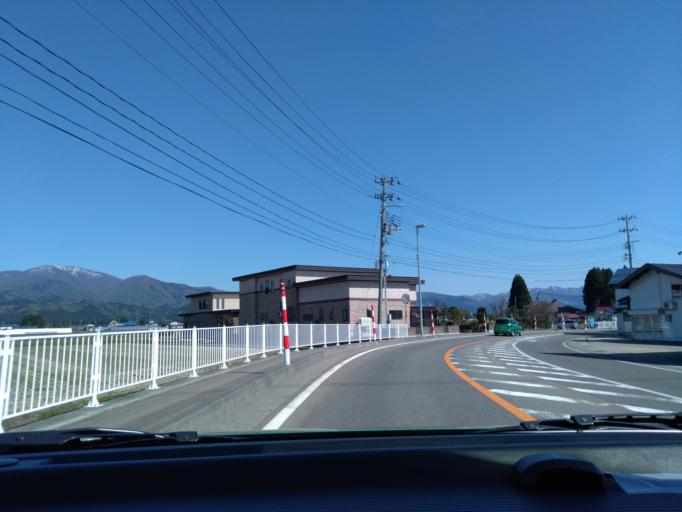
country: JP
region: Akita
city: Kakunodatemachi
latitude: 39.5713
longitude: 140.5803
